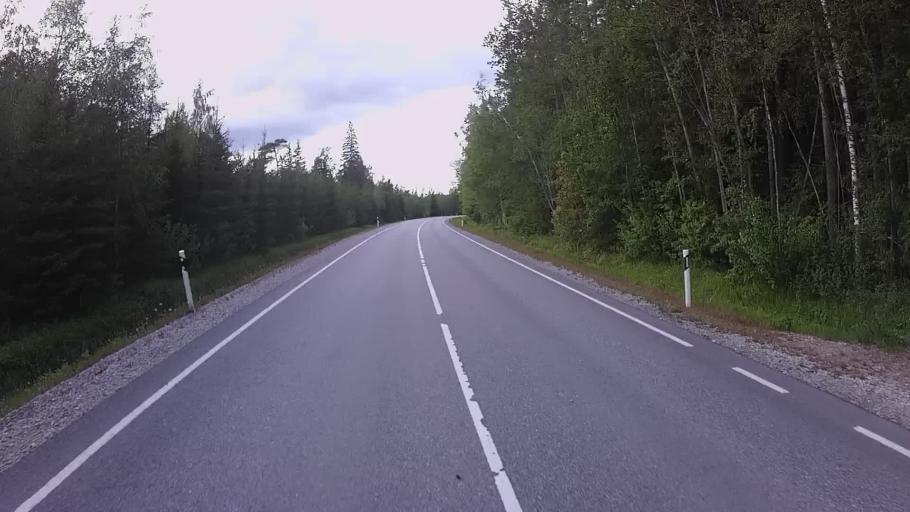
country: EE
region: Jogevamaa
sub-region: Mustvee linn
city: Mustvee
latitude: 58.8704
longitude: 26.8261
